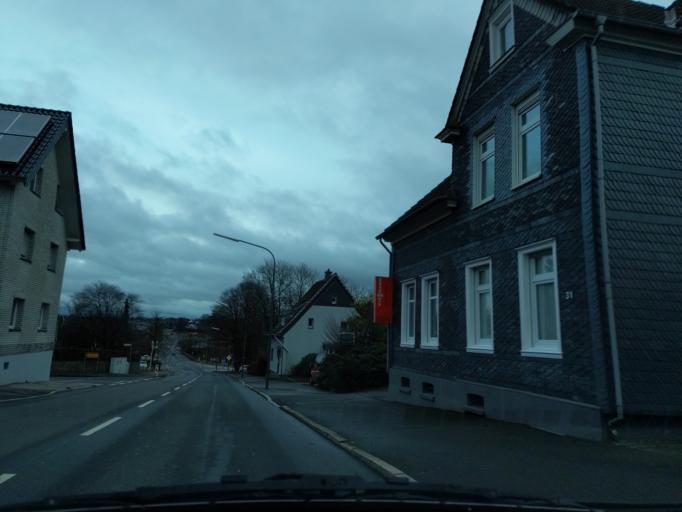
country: DE
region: North Rhine-Westphalia
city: Wermelskirchen
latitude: 51.1384
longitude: 7.1870
